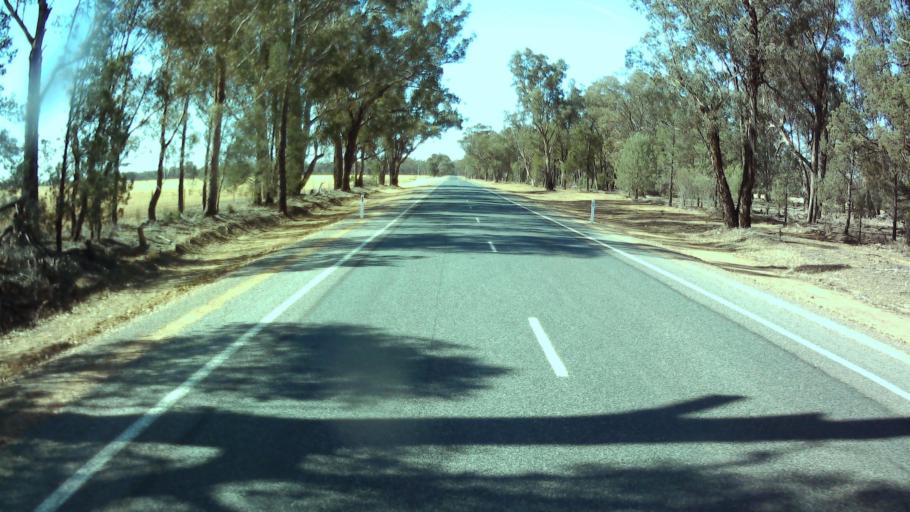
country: AU
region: New South Wales
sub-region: Weddin
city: Grenfell
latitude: -33.7385
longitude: 148.0887
